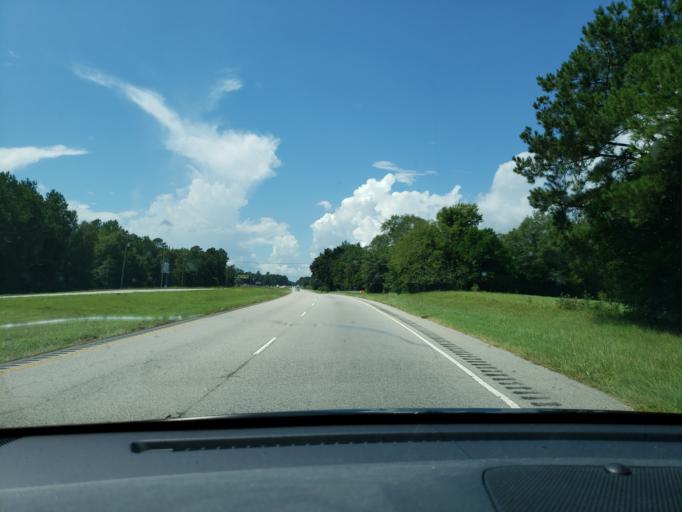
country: US
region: North Carolina
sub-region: Bladen County
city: Elizabethtown
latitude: 34.6455
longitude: -78.6885
